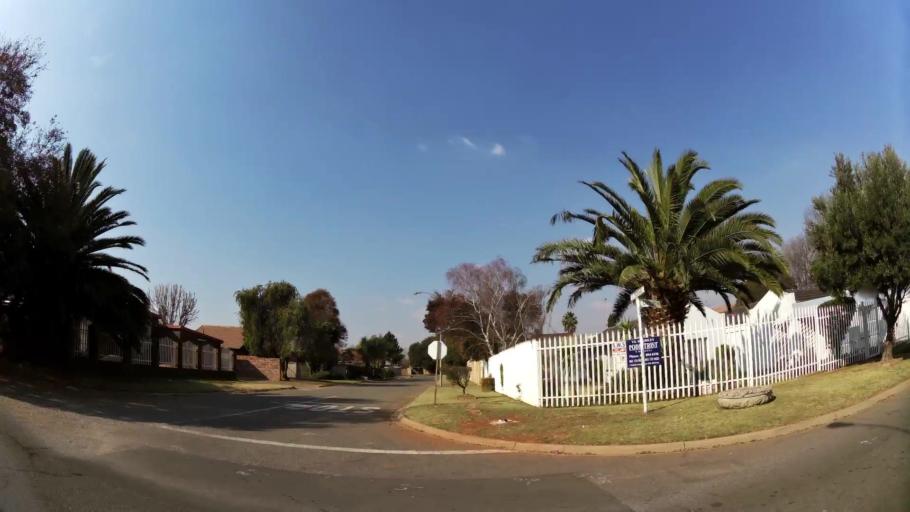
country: ZA
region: Gauteng
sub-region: Ekurhuleni Metropolitan Municipality
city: Boksburg
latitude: -26.1860
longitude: 28.2633
